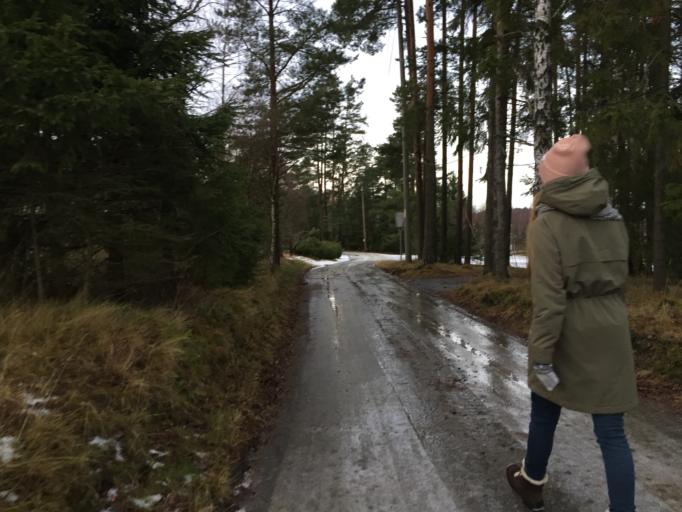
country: NO
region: Ostfold
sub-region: Moss
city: Moss
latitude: 59.4892
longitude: 10.6715
